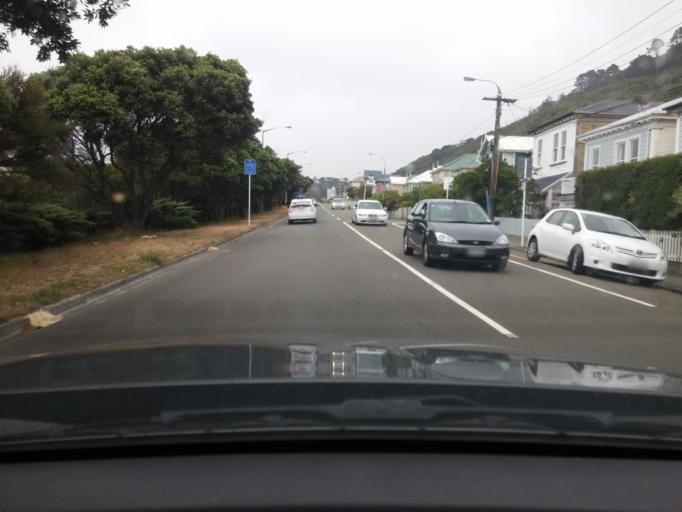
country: NZ
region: Wellington
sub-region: Wellington City
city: Wellington
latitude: -41.2731
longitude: 174.7759
